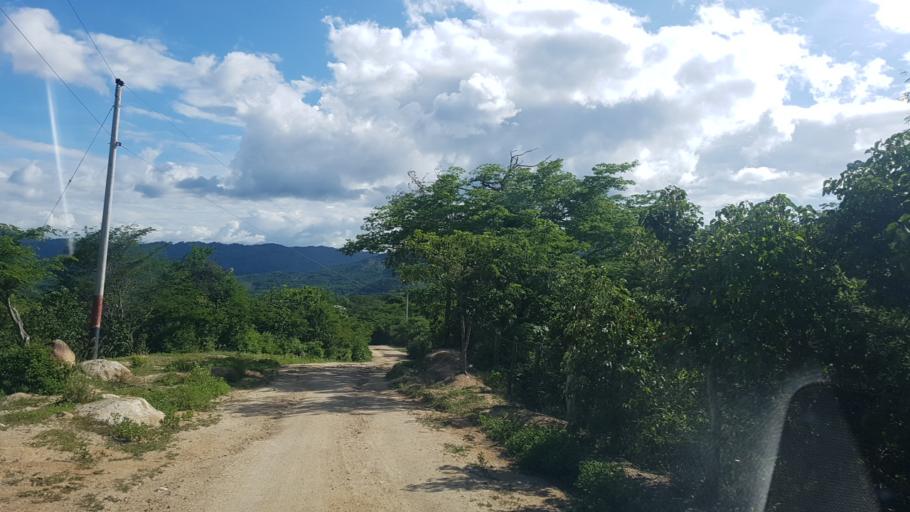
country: NI
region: Nueva Segovia
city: Mozonte
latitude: 13.6395
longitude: -86.3981
